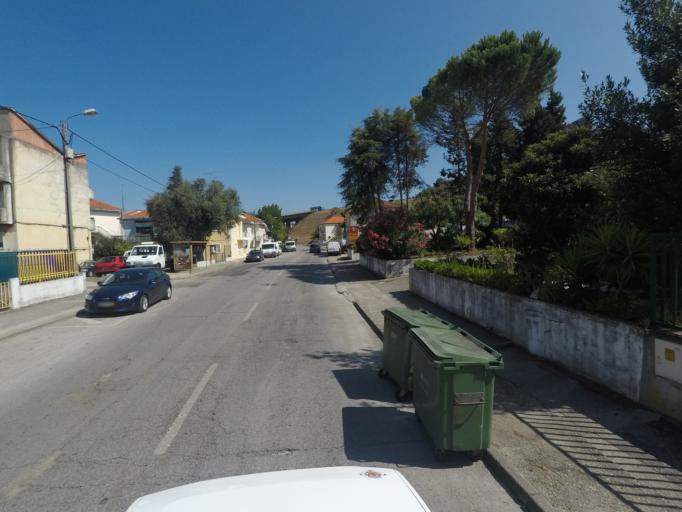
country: PT
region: Coimbra
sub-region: Coimbra
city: Coimbra
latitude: 40.2305
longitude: -8.4368
